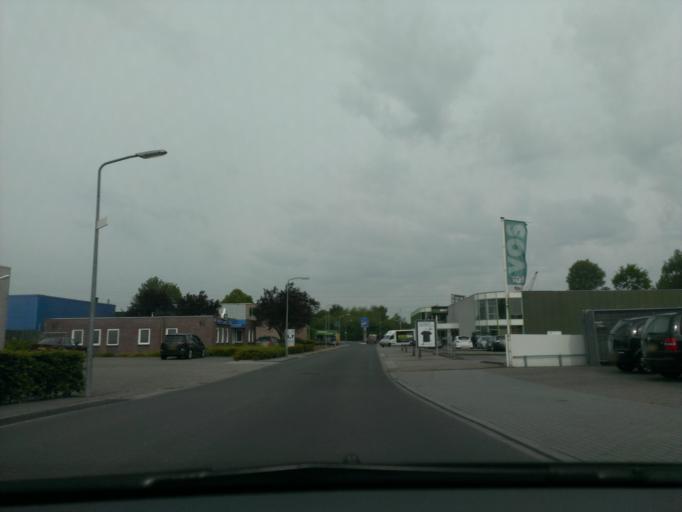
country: NL
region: Overijssel
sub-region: Gemeente Almelo
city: Almelo
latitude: 52.3350
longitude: 6.6575
